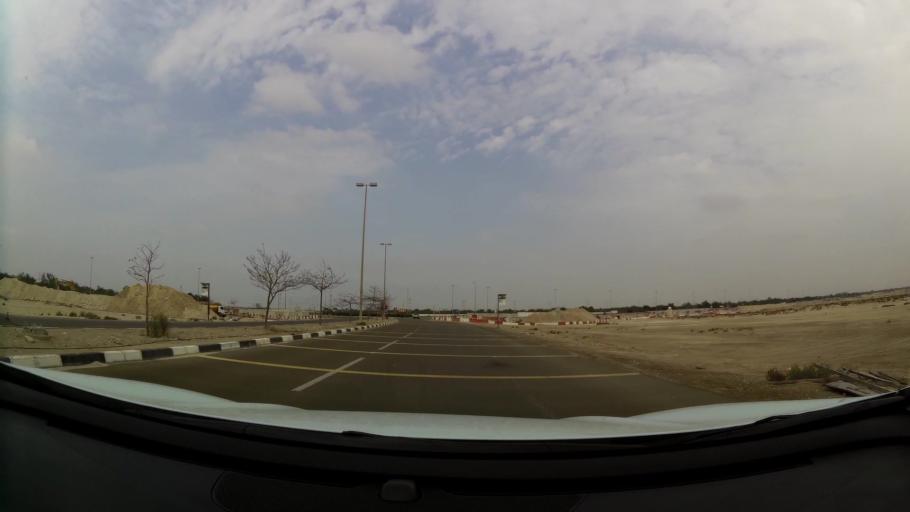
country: AE
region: Abu Dhabi
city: Abu Dhabi
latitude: 24.6272
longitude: 54.7081
